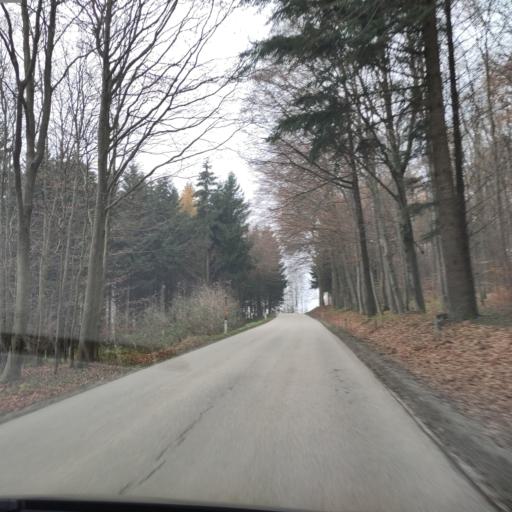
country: AT
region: Lower Austria
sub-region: Politischer Bezirk Sankt Polten
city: Neidling
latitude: 48.2640
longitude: 15.5104
